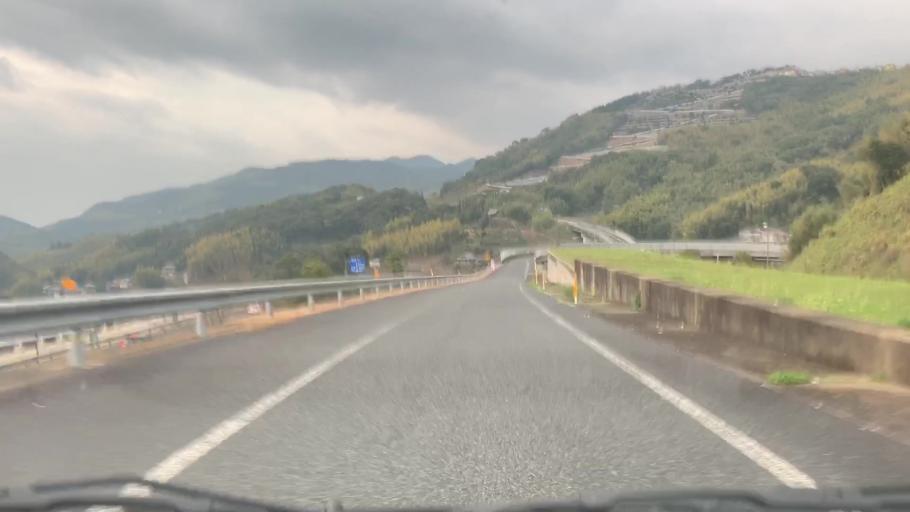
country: JP
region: Nagasaki
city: Nagasaki-shi
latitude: 32.7291
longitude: 129.9059
